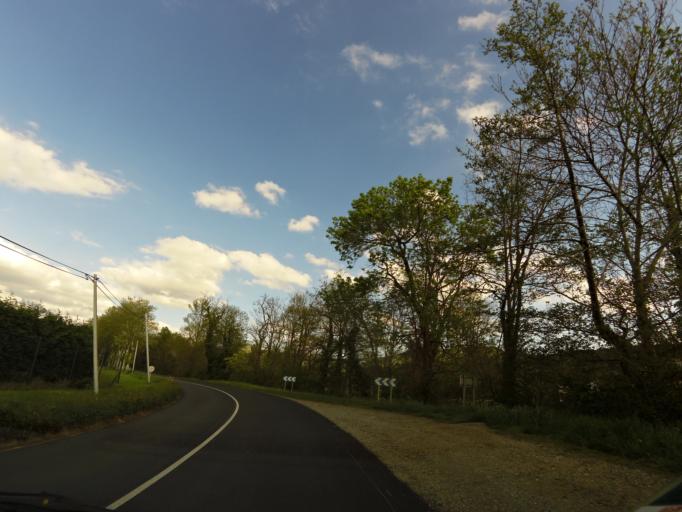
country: FR
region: Midi-Pyrenees
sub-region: Departement du Tarn
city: Soreze
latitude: 43.4516
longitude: 2.0382
